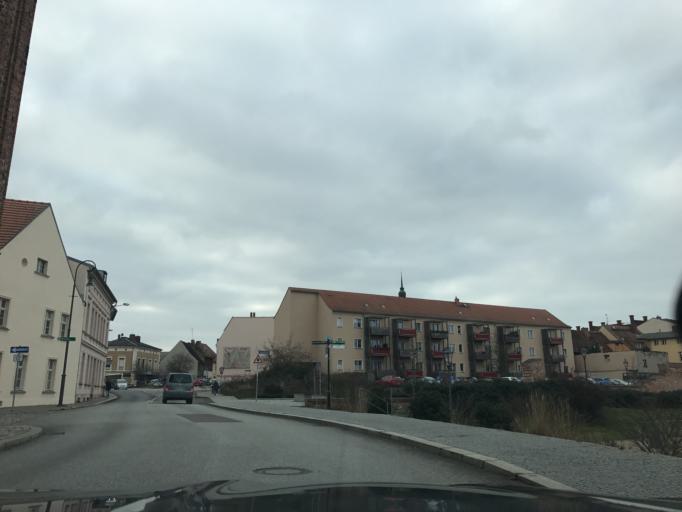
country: DE
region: Brandenburg
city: Brandenburg an der Havel
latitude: 52.4111
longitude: 12.5648
